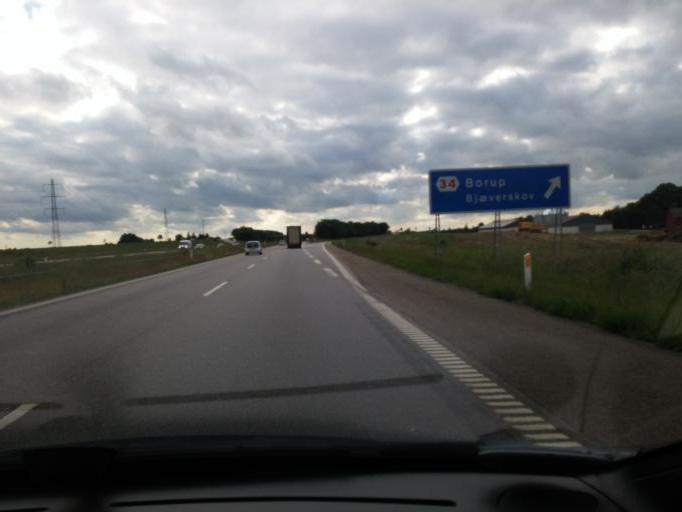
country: DK
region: Zealand
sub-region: Koge Kommune
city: Borup
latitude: 55.4580
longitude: 11.9917
